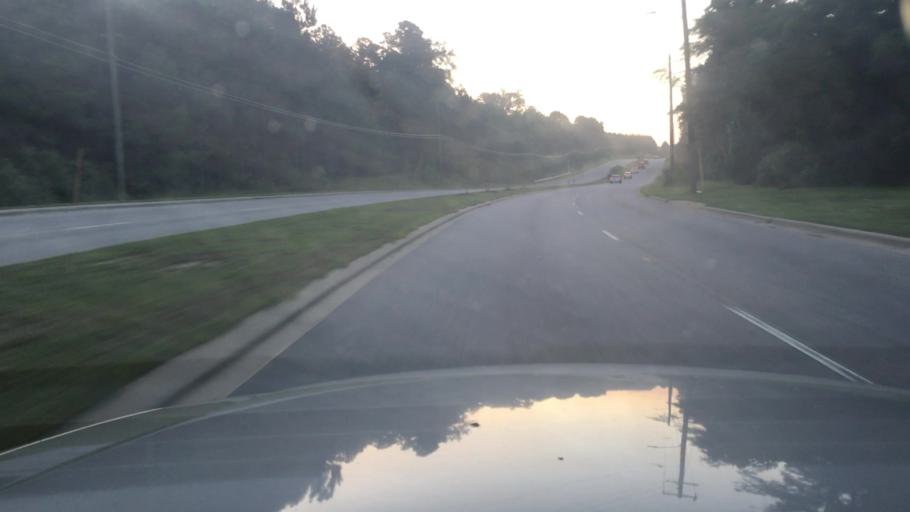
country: US
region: North Carolina
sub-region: Hoke County
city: Rockfish
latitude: 35.0649
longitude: -79.0347
